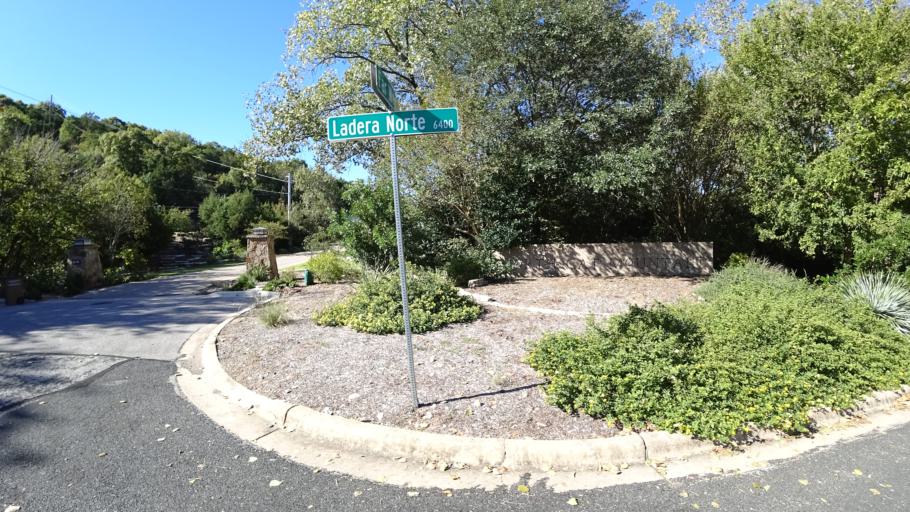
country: US
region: Texas
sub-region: Travis County
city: West Lake Hills
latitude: 30.3589
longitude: -97.7806
